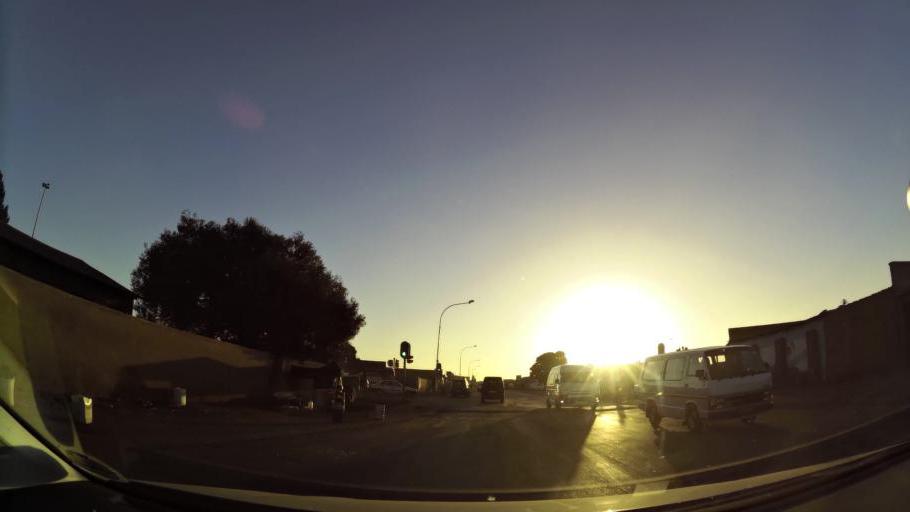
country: ZA
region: Gauteng
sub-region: Ekurhuleni Metropolitan Municipality
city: Tembisa
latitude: -25.9960
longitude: 28.2302
